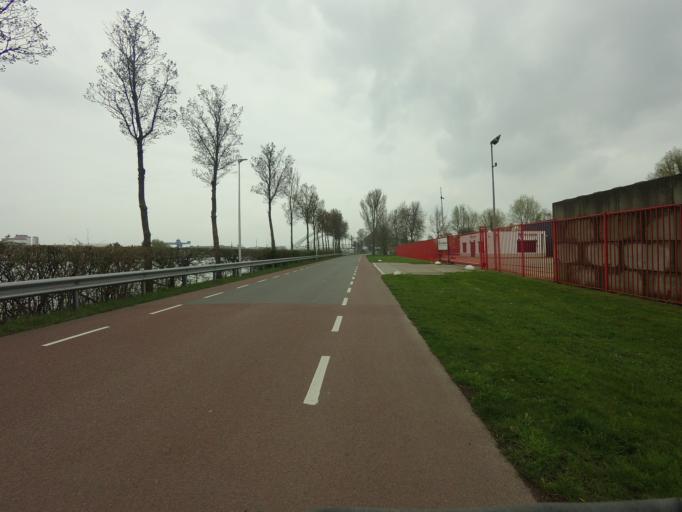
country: NL
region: Utrecht
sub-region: Gemeente Utrecht
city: Utrecht
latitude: 52.1046
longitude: 5.0775
